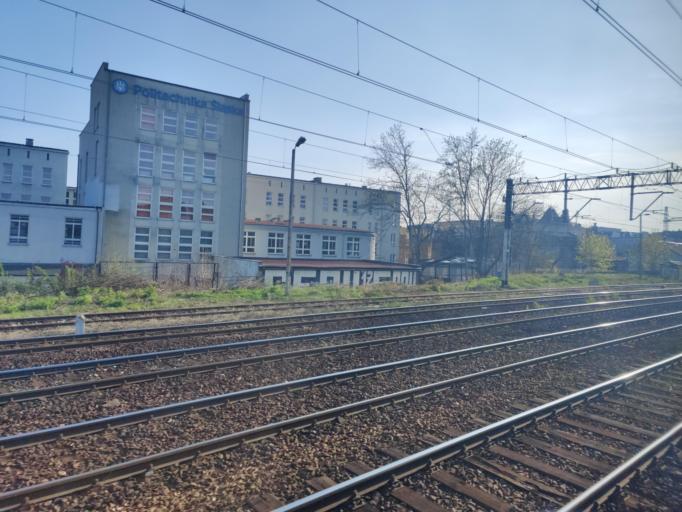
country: PL
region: Silesian Voivodeship
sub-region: Katowice
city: Katowice
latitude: 50.2567
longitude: 19.0335
